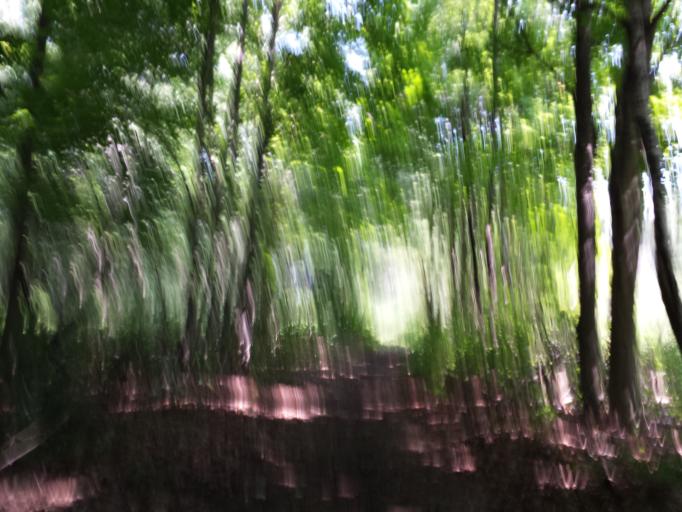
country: US
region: Vermont
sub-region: Rutland County
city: Castleton
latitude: 43.6016
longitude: -73.1818
